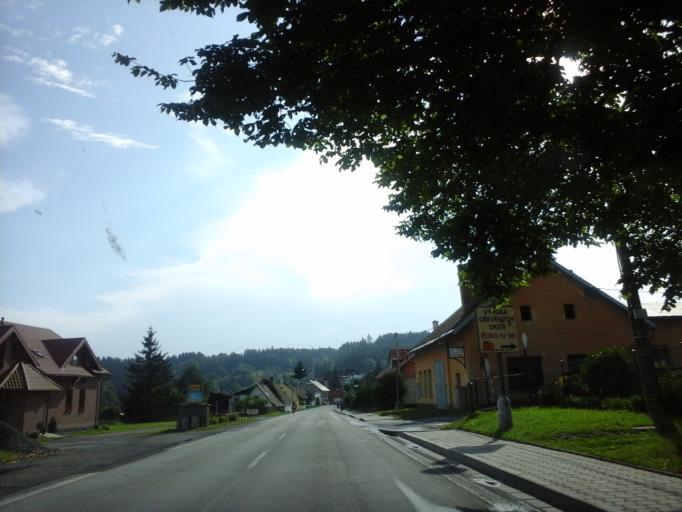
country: CZ
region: Olomoucky
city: Stity
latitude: 49.9636
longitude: 16.7720
